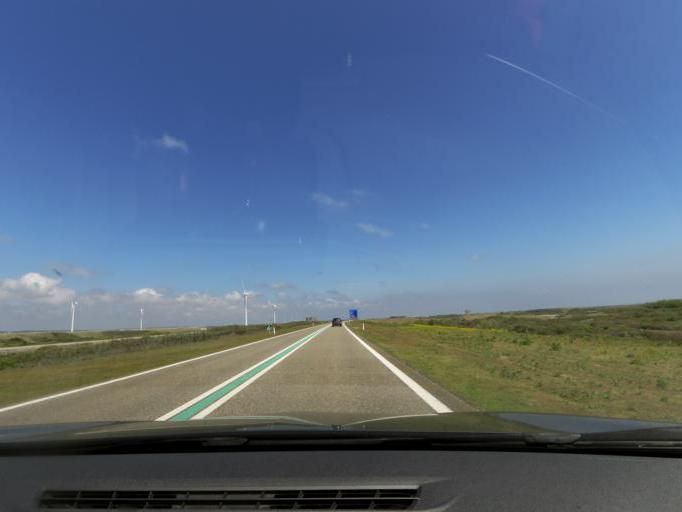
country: NL
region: Zeeland
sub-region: Gemeente Noord-Beveland
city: Kamperland
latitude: 51.6304
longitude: 3.6953
